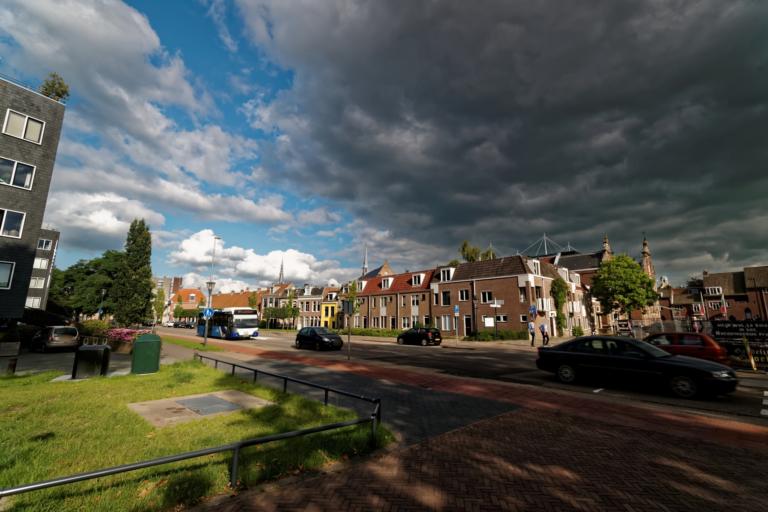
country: NL
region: Friesland
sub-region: Gemeente Leeuwarden
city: Bilgaard
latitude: 53.2047
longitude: 5.7951
